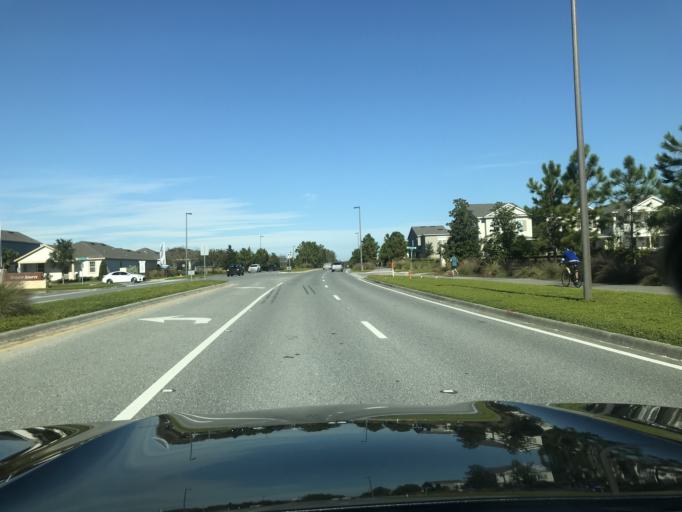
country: US
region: Florida
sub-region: Orange County
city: Oakland
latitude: 28.4632
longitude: -81.6261
